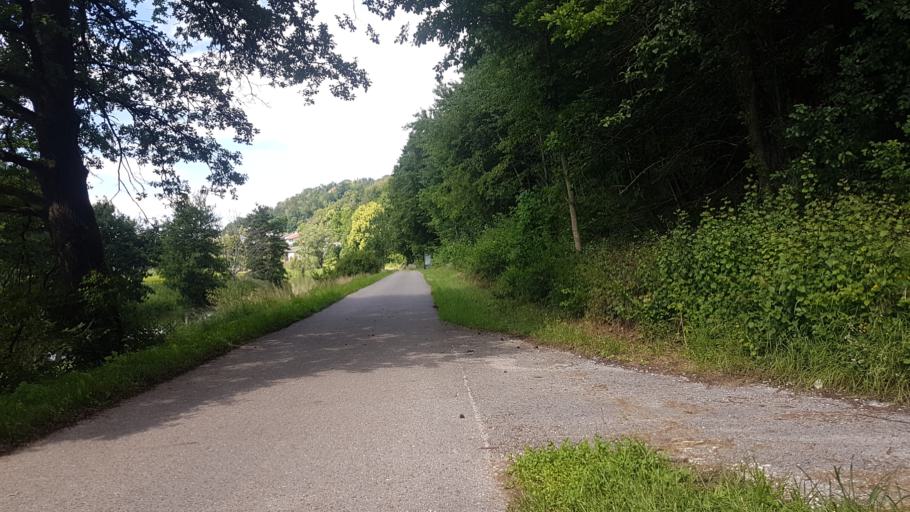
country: DE
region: Bavaria
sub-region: Regierungsbezirk Mittelfranken
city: Treuchtlingen
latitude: 48.9397
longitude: 10.9331
